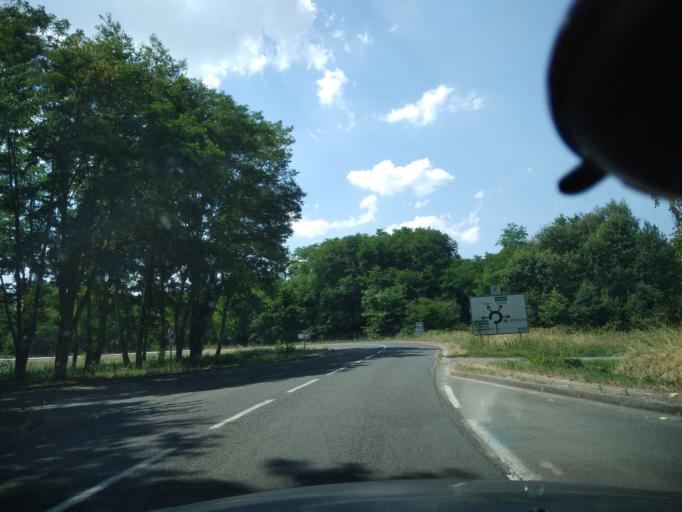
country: FR
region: Centre
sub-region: Departement d'Indre-et-Loire
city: Civray-de-Touraine
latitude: 47.3228
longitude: 1.0365
